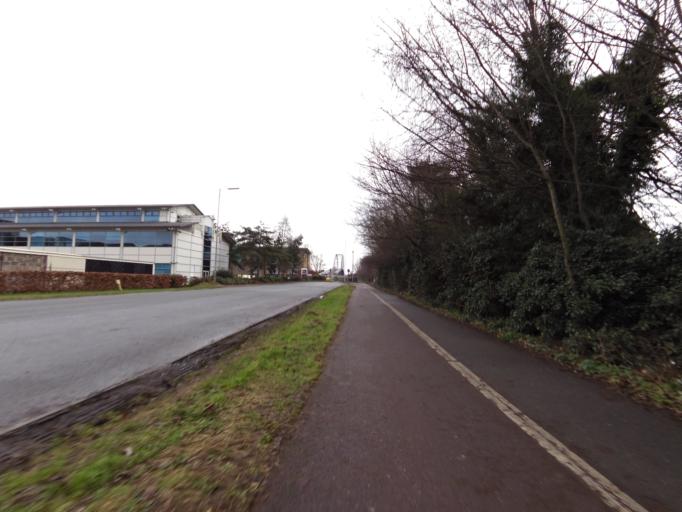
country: GB
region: England
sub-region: Cambridgeshire
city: Waterbeach
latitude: 52.2349
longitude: 0.1544
